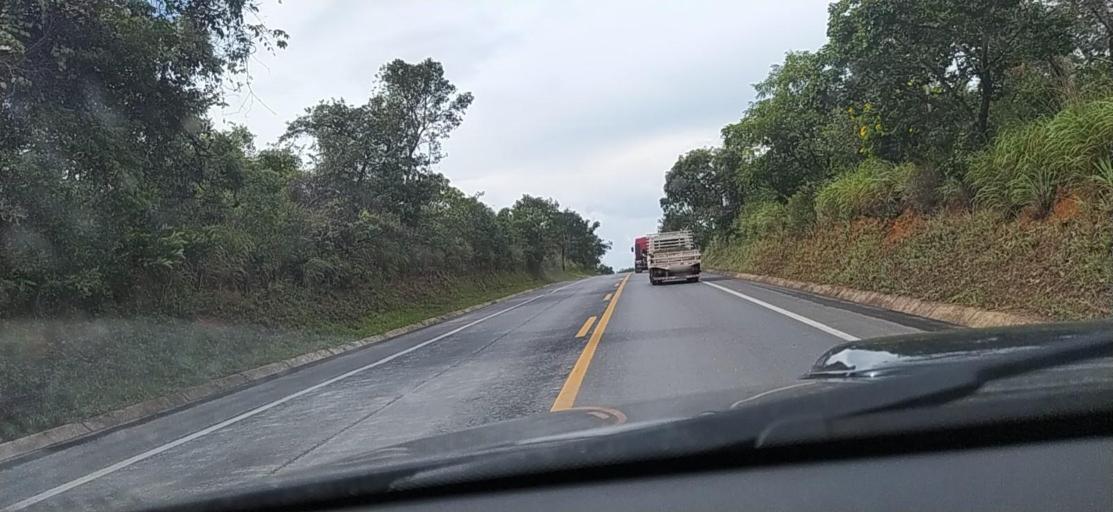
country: BR
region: Minas Gerais
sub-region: Montes Claros
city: Montes Claros
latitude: -16.8501
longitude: -43.8521
